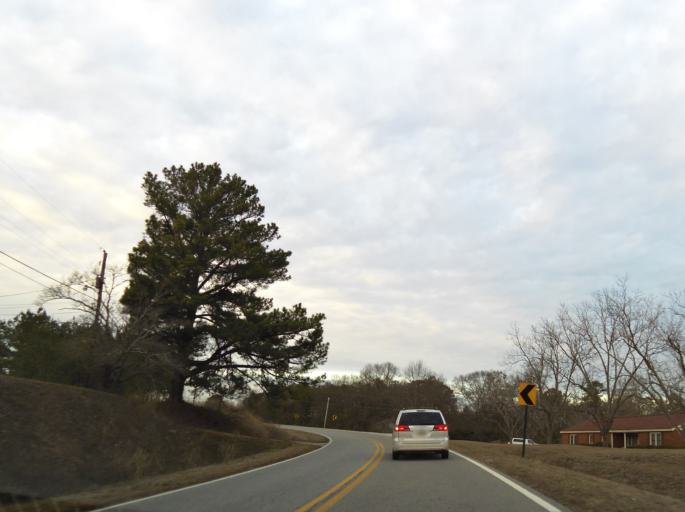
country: US
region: Georgia
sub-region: Peach County
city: Byron
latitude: 32.7253
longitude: -83.7189
